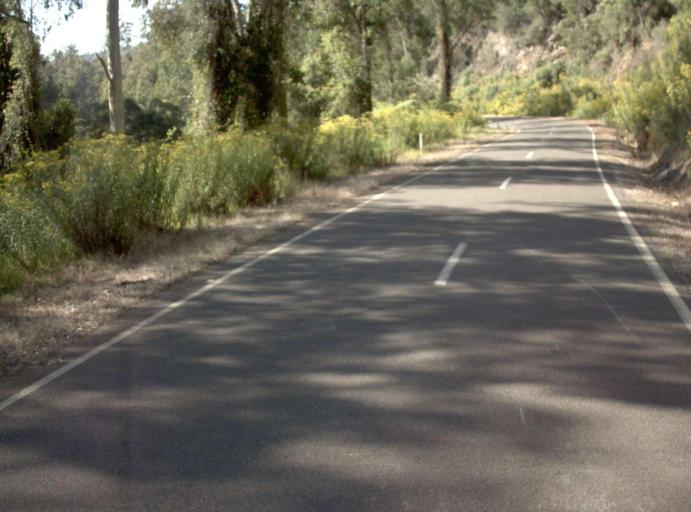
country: AU
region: Victoria
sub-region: East Gippsland
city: Lakes Entrance
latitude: -37.5265
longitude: 148.5293
